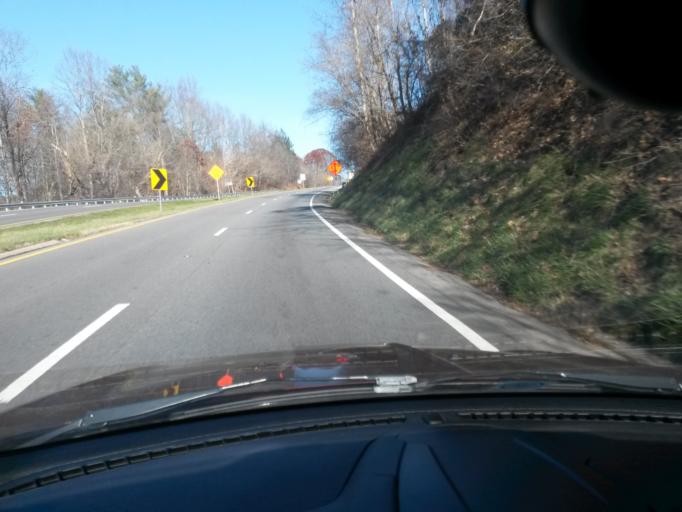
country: US
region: Virginia
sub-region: Roanoke County
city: Narrows
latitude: 37.1732
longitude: -79.9416
